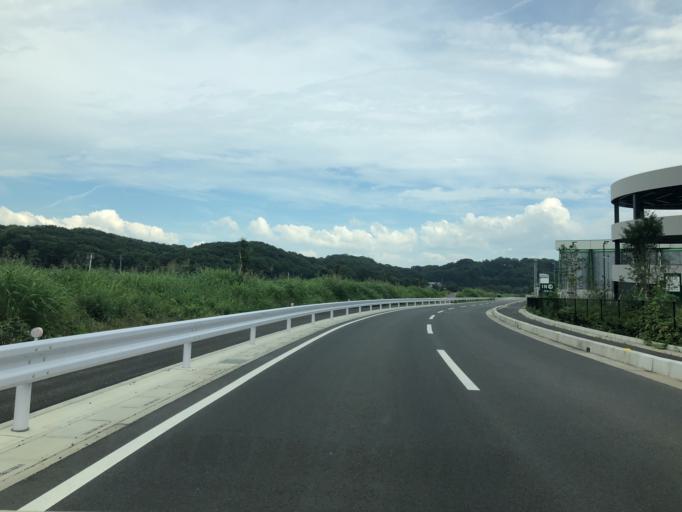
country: JP
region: Saitama
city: Fukiage-fujimi
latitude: 36.0446
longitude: 139.4163
